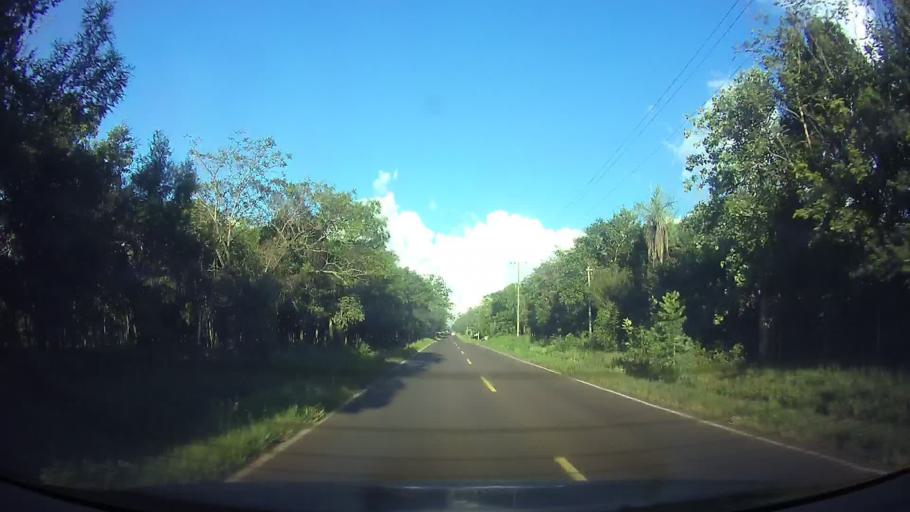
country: PY
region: Cordillera
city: Emboscada
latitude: -25.2025
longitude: -57.3322
